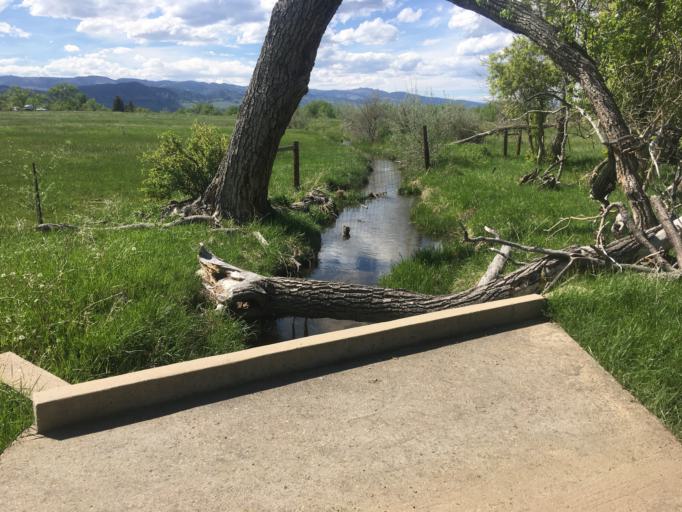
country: US
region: Colorado
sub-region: Boulder County
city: Superior
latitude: 39.9871
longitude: -105.2081
